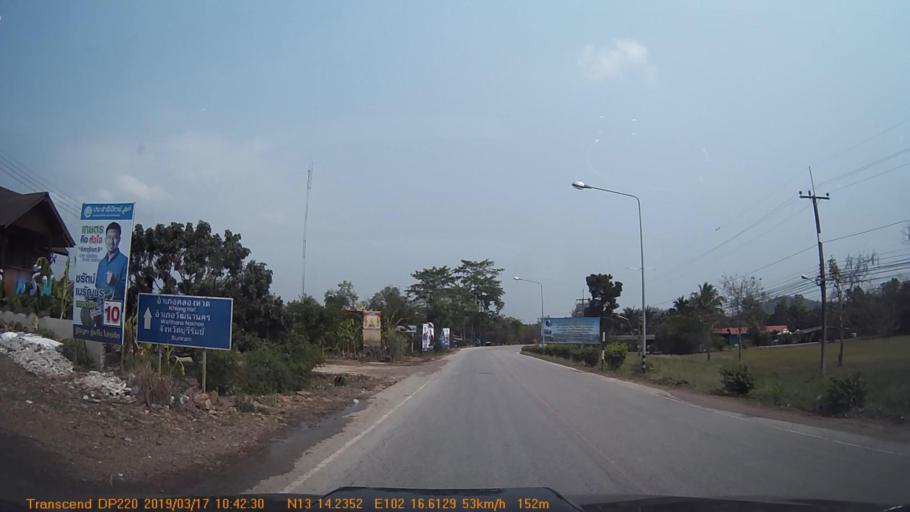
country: TH
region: Chanthaburi
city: Soi Dao
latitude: 13.2375
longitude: 102.2769
